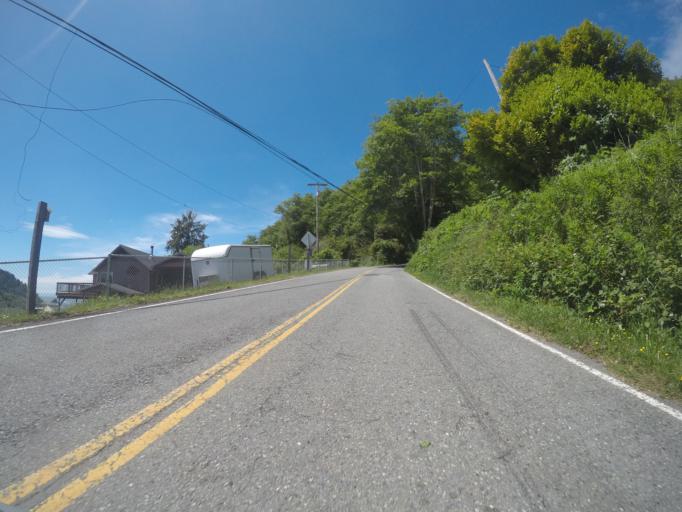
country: US
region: California
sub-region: Del Norte County
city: Bertsch-Oceanview
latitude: 41.5465
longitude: -124.0667
